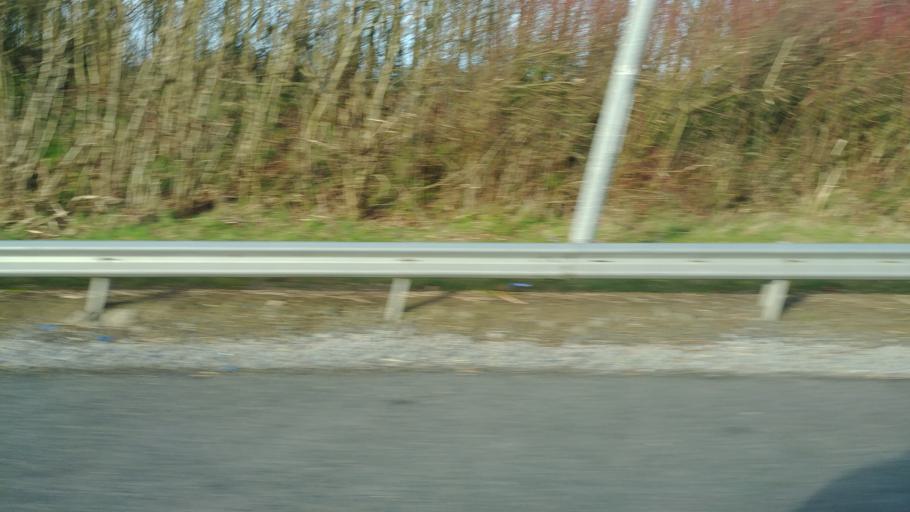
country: IE
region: Leinster
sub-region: Lu
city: Dromiskin
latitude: 53.9261
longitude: -6.4134
